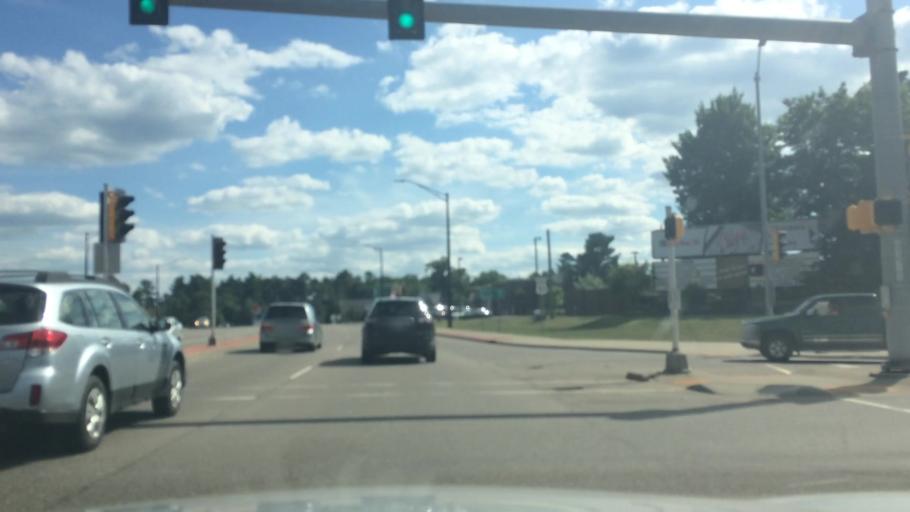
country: US
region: Wisconsin
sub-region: Vilas County
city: Lac du Flambeau
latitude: 45.8877
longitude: -89.7037
